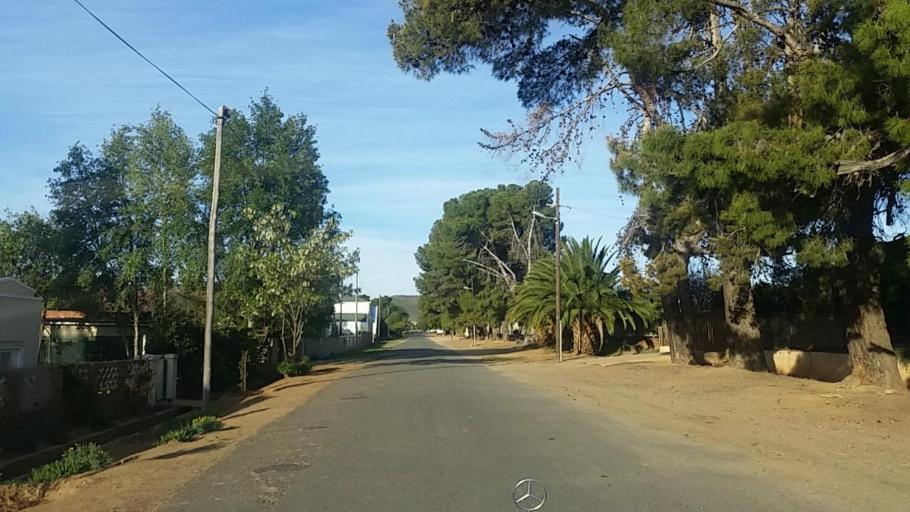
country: ZA
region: Western Cape
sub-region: Eden District Municipality
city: Knysna
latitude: -33.6550
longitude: 23.1265
